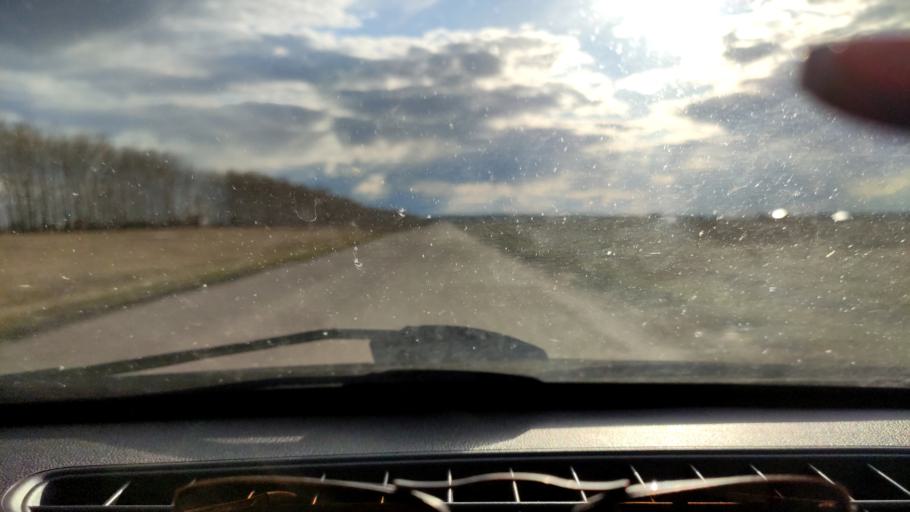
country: RU
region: Bashkortostan
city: Karmaskaly
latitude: 54.3510
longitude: 56.1294
